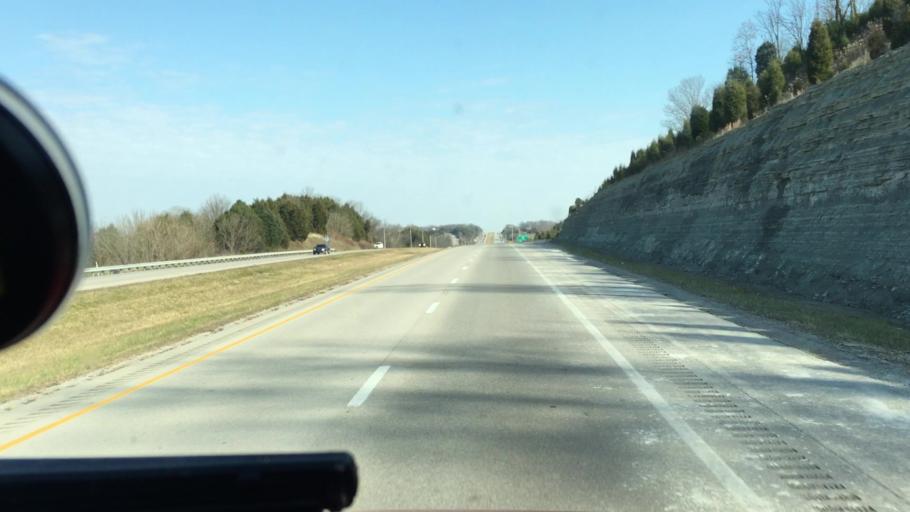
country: US
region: Kentucky
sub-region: Bath County
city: Owingsville
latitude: 38.1351
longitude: -83.7326
